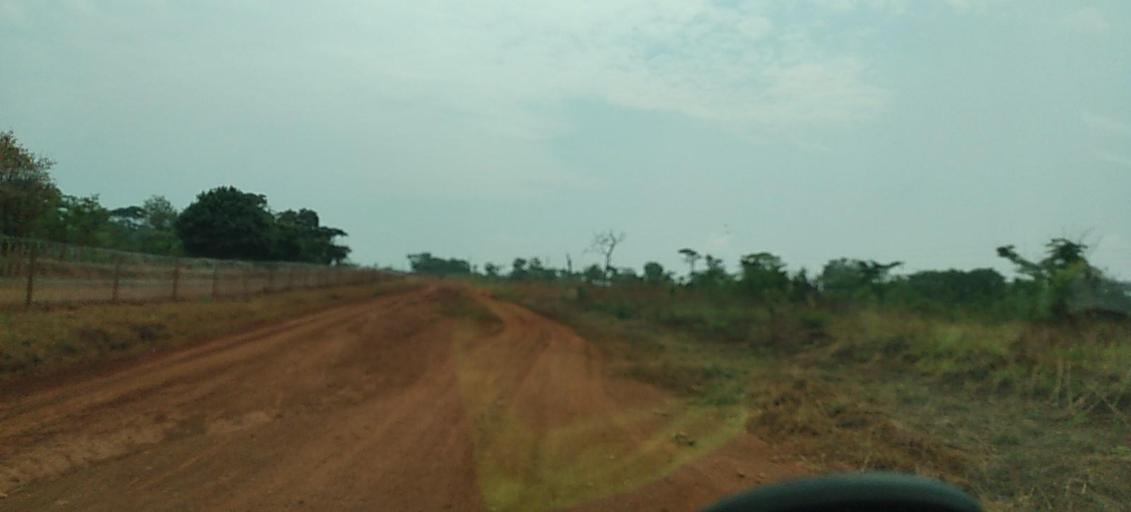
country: ZM
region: North-Western
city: Kansanshi
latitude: -12.0991
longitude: 26.4915
